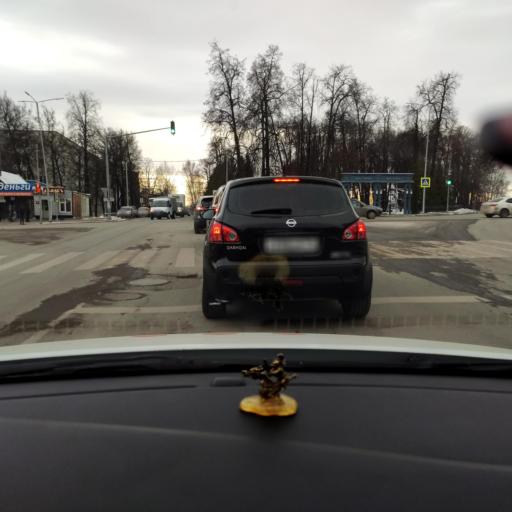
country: RU
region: Tatarstan
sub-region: Zelenodol'skiy Rayon
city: Zelenodolsk
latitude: 55.8469
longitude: 48.5011
